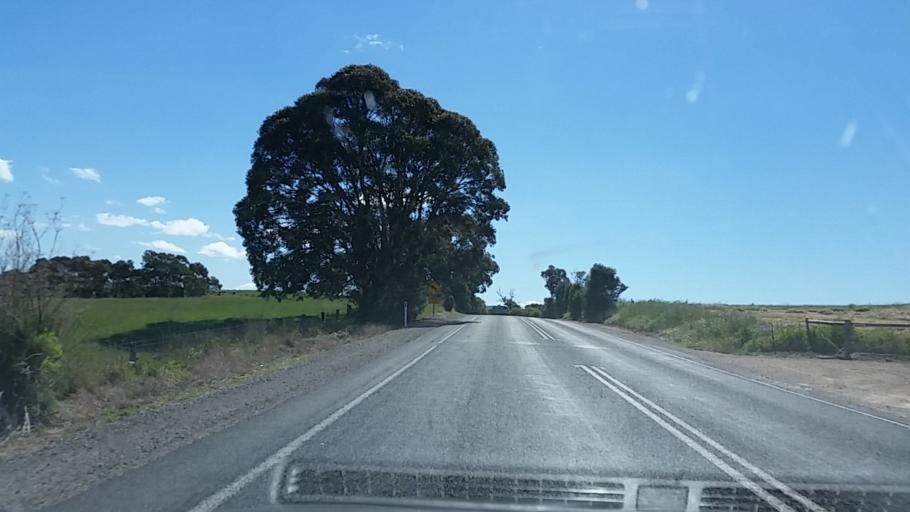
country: AU
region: South Australia
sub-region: Alexandrina
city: Strathalbyn
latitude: -35.2423
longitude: 138.8756
